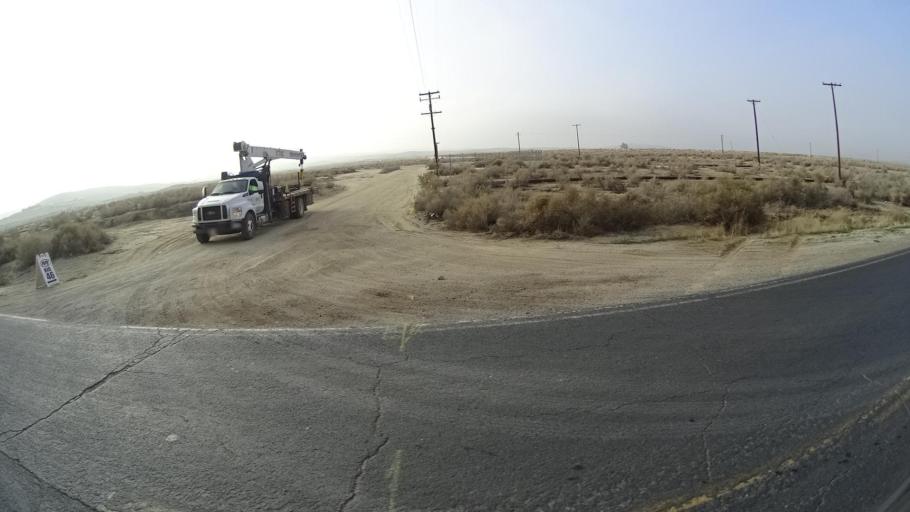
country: US
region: California
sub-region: Kern County
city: Ford City
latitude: 35.2095
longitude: -119.4456
